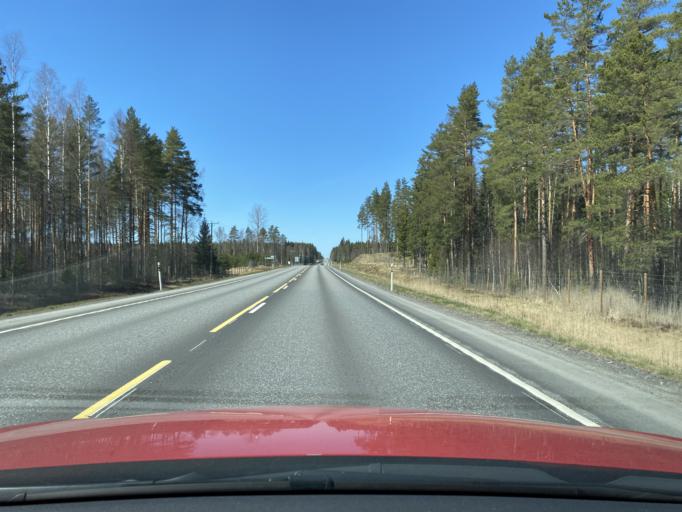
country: FI
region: Uusimaa
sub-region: Helsinki
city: Kaerkoelae
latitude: 60.6474
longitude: 23.8709
